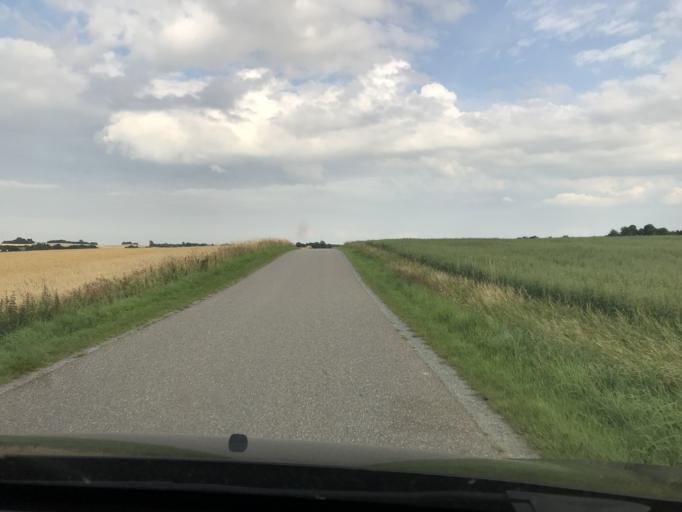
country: DK
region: South Denmark
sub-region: Vejle Kommune
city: Jelling
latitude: 55.8038
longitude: 9.4412
